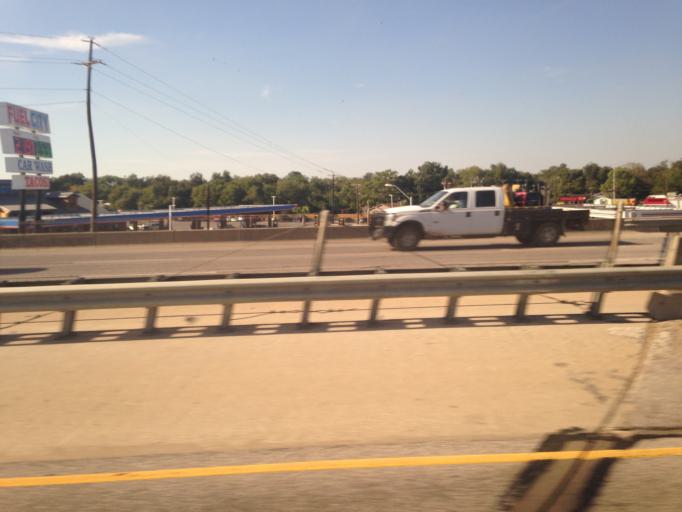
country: US
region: Texas
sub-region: Tarrant County
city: Haltom City
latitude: 32.7813
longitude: -97.2737
